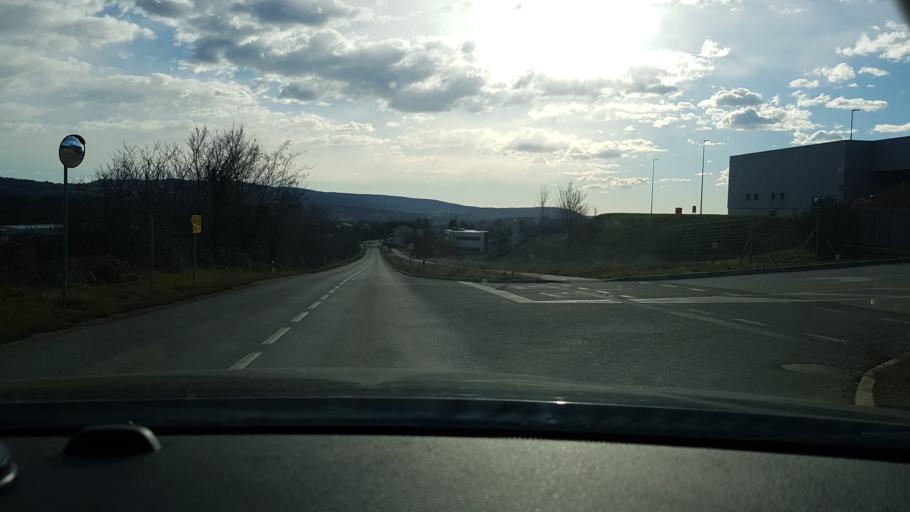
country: HR
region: Istarska
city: Vinez
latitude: 45.1111
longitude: 14.1105
